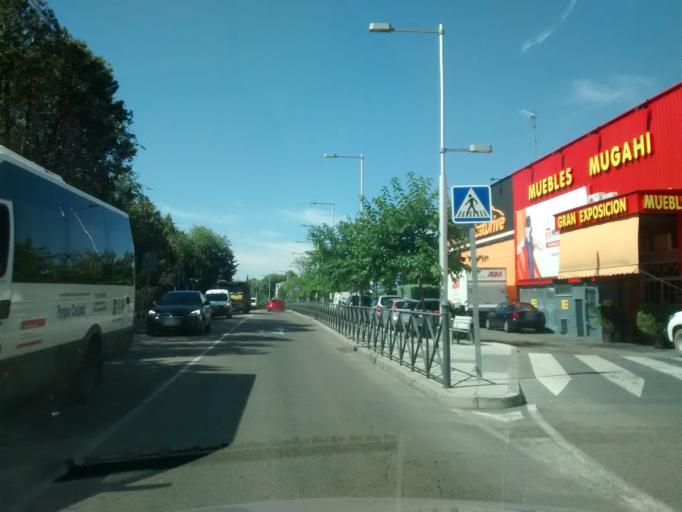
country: ES
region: Madrid
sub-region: Provincia de Madrid
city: San Fernando de Henares
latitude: 40.4377
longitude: -3.5323
